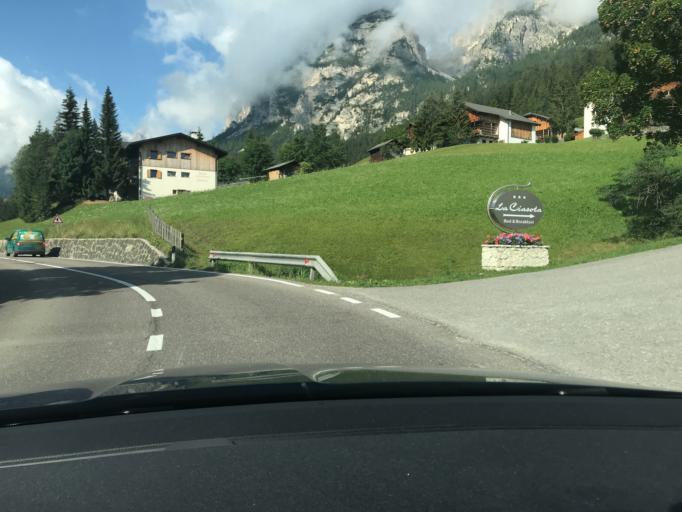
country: IT
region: Trentino-Alto Adige
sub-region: Bolzano
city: Badia
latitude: 46.5803
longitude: 11.8991
